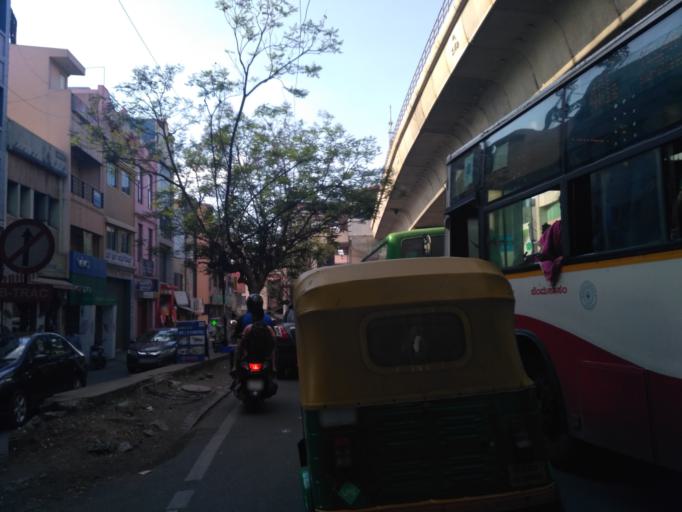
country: IN
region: Karnataka
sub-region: Bangalore Urban
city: Bangalore
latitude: 13.0069
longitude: 77.5485
